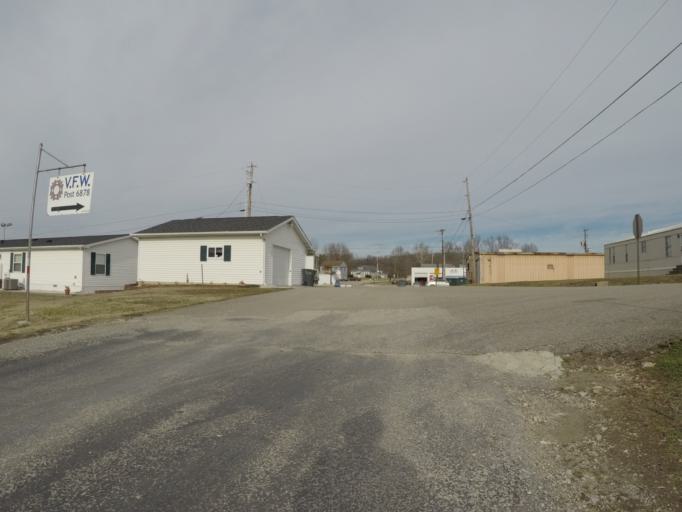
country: US
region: West Virginia
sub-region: Cabell County
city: Pea Ridge
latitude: 38.4402
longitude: -82.3650
